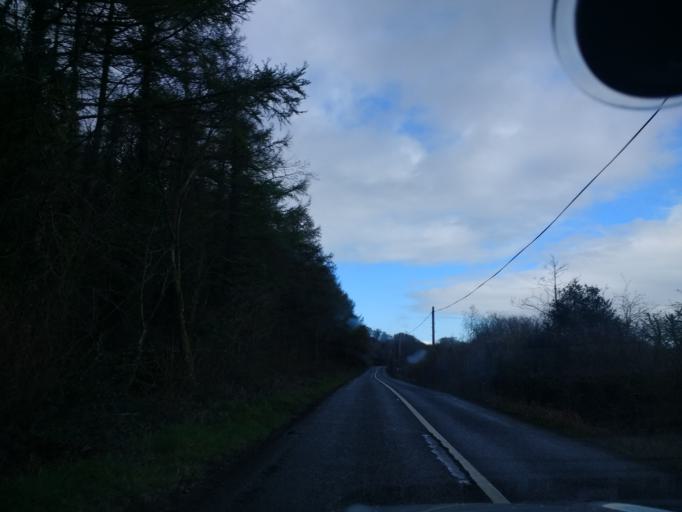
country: IE
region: Ulster
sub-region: County Donegal
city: Buncrana
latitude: 55.1238
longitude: -7.5286
